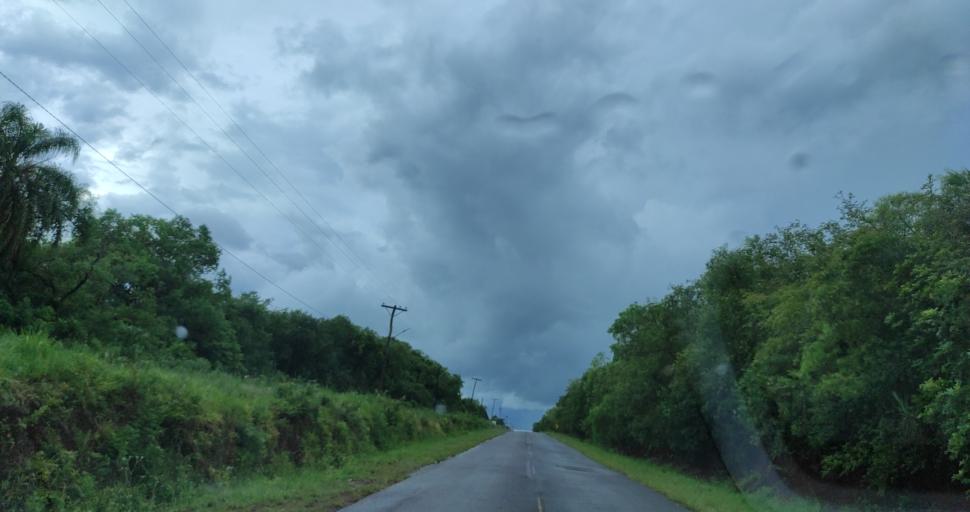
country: AR
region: Misiones
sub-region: Departamento de Apostoles
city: San Jose
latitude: -27.7717
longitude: -55.7655
